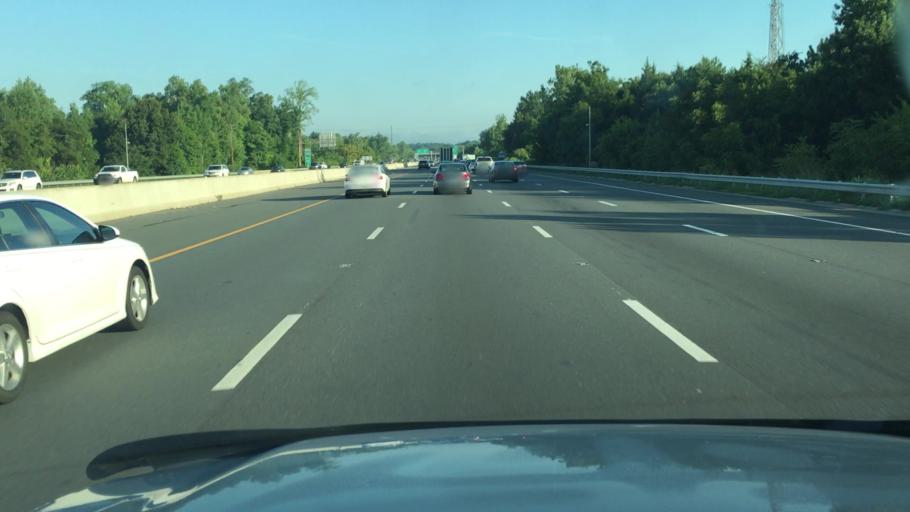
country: US
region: North Carolina
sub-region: Mecklenburg County
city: Pineville
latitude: 35.1103
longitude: -80.8964
